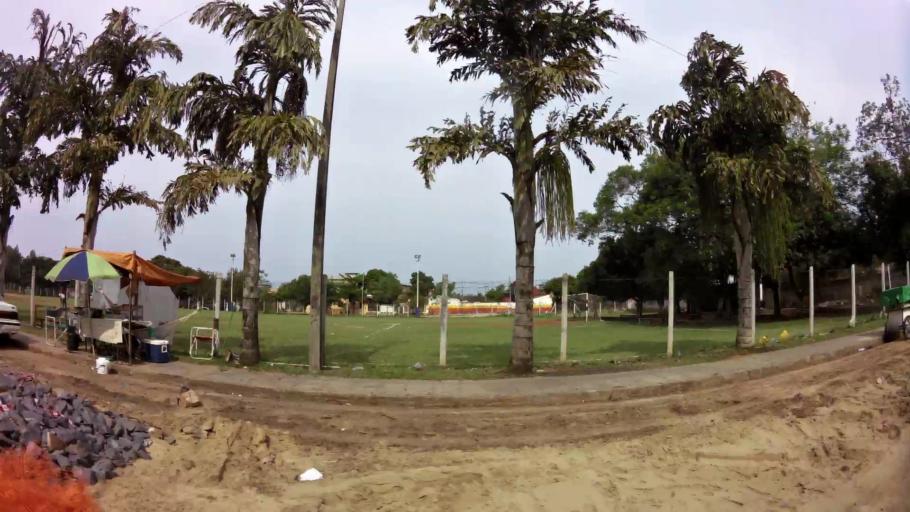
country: PY
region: Central
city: Fernando de la Mora
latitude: -25.3040
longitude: -57.5543
